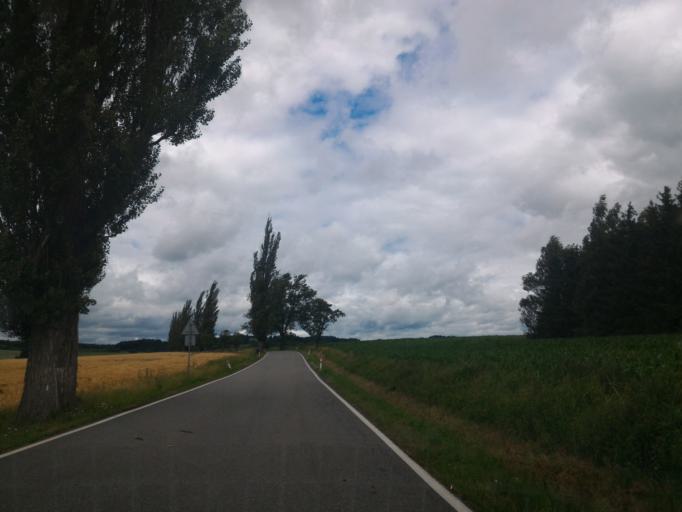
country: CZ
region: Vysocina
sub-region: Okres Jihlava
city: Telc
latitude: 49.2001
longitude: 15.4391
